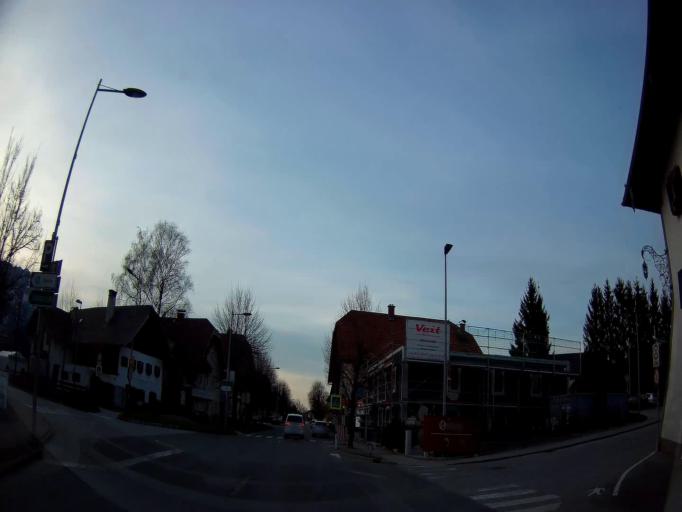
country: AT
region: Salzburg
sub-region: Politischer Bezirk Hallein
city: Oberalm
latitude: 47.7000
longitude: 13.0991
